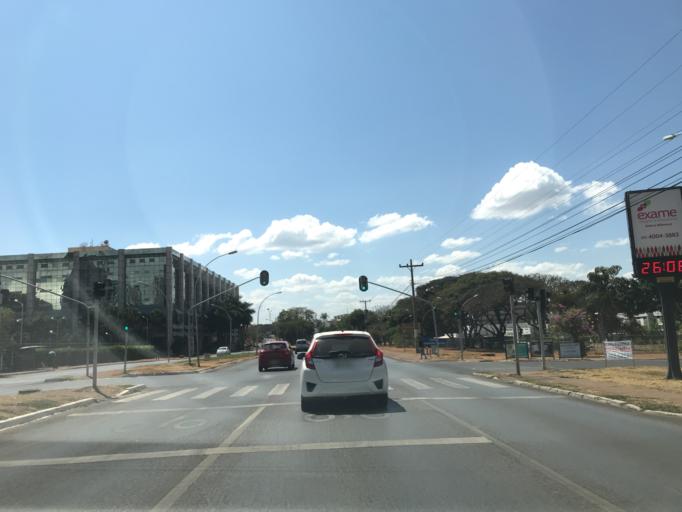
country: BR
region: Federal District
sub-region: Brasilia
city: Brasilia
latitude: -15.7860
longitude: -47.8877
